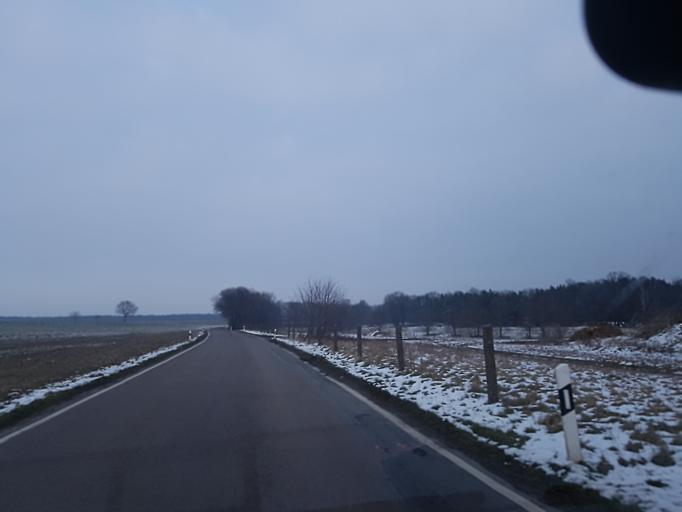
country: DE
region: Saxony
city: Cavertitz
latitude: 51.3894
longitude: 13.1614
